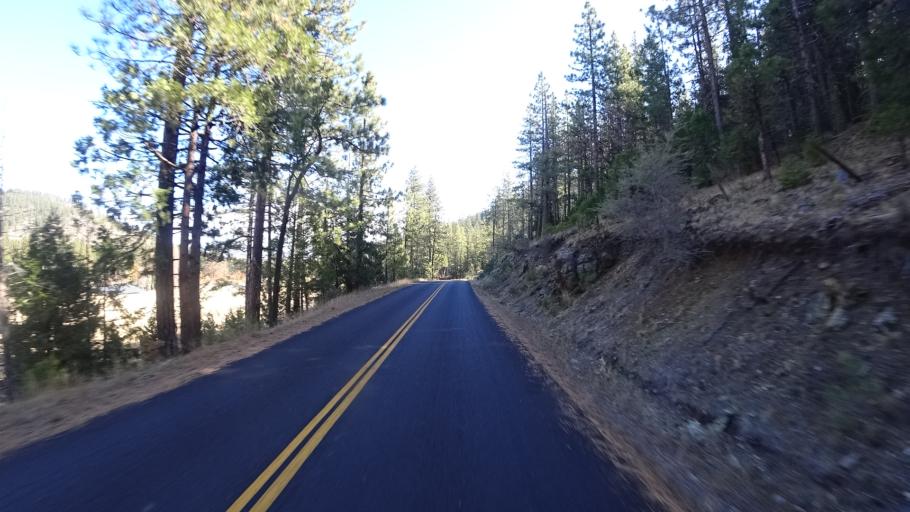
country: US
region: California
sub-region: Siskiyou County
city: Weed
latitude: 41.4326
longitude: -122.4856
